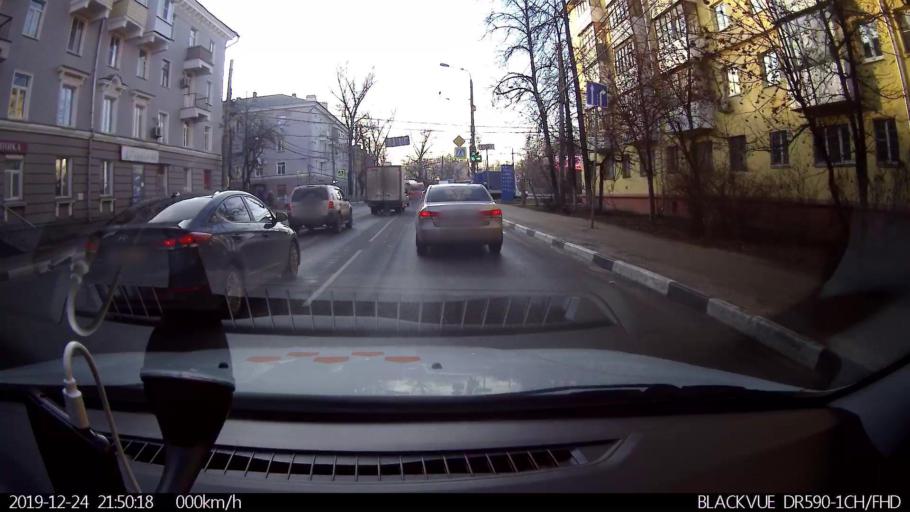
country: RU
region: Nizjnij Novgorod
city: Nizhniy Novgorod
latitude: 56.3269
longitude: 43.9540
